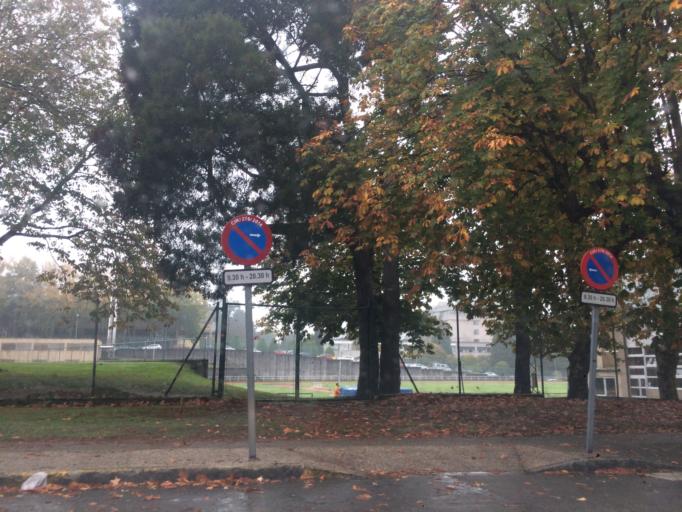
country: ES
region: Galicia
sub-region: Provincia da Coruna
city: Santiago de Compostela
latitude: 42.8763
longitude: -8.5558
